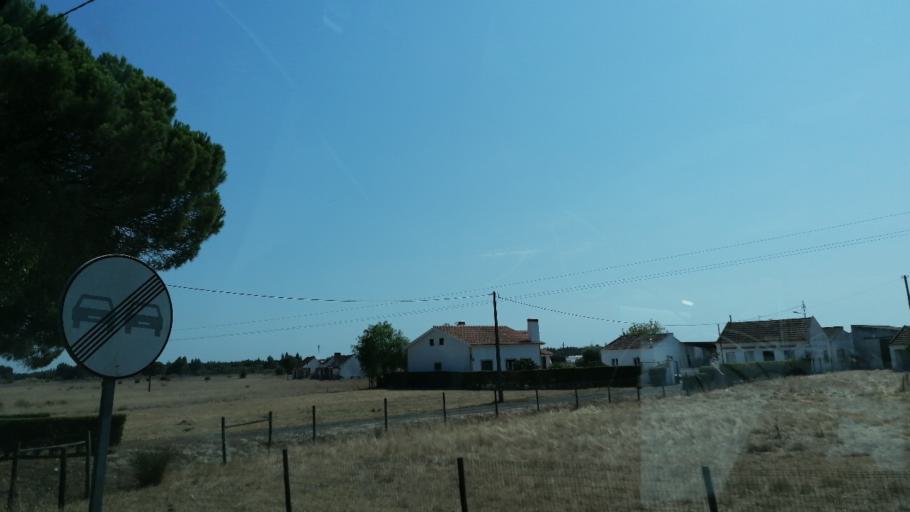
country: PT
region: Santarem
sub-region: Benavente
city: Poceirao
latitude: 38.7386
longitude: -8.6559
